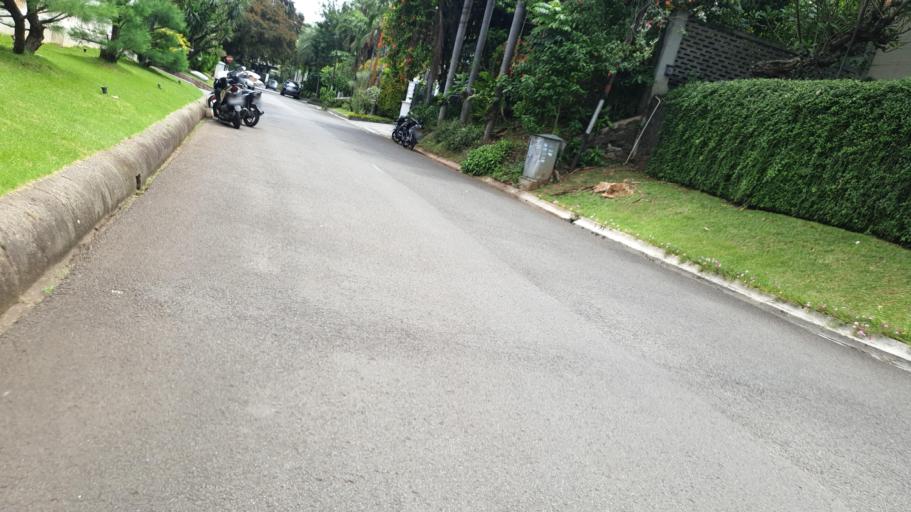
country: ID
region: Banten
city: South Tangerang
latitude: -6.2792
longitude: 106.7872
